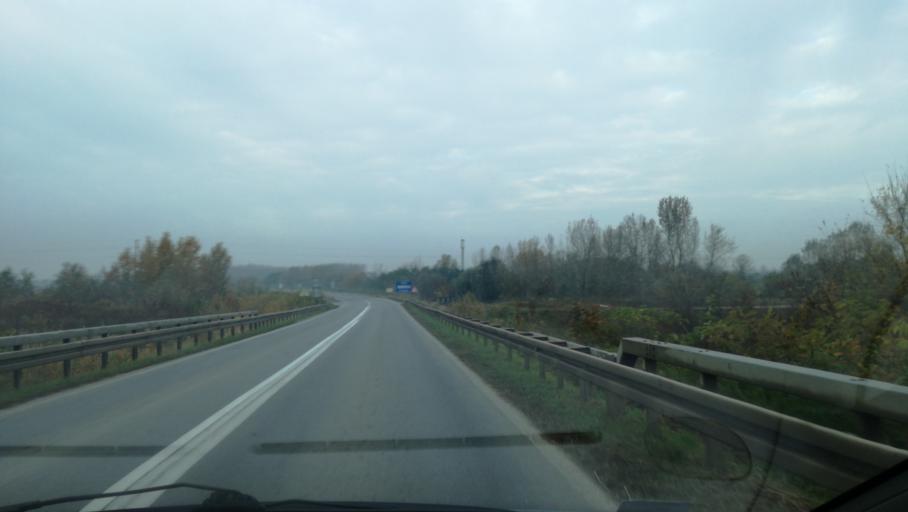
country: RS
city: Taras
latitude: 45.3987
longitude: 20.2097
